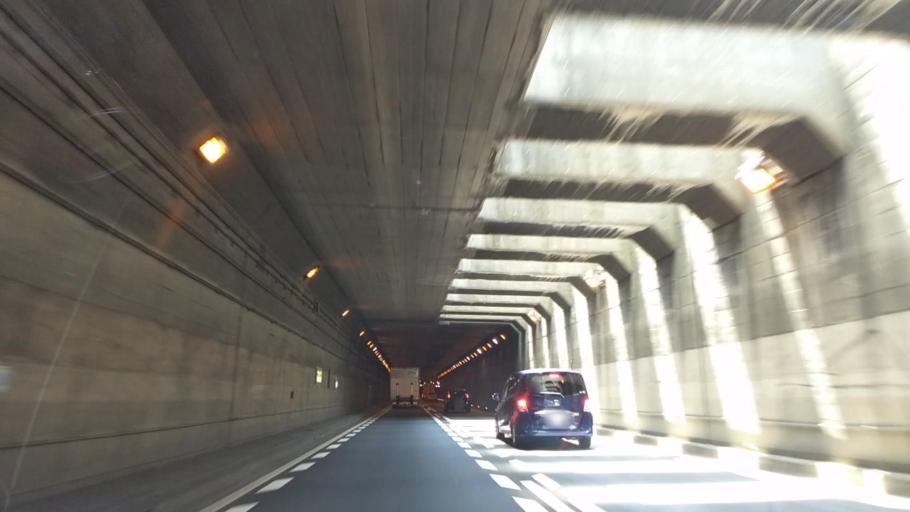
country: JP
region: Kanagawa
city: Minami-rinkan
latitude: 35.4899
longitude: 139.4628
